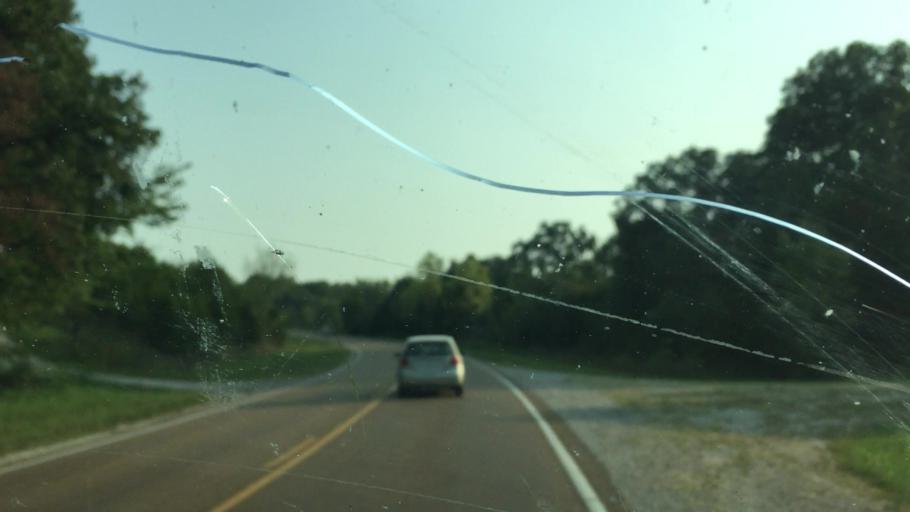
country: US
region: Missouri
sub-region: Pulaski County
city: Richland
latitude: 37.8177
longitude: -92.4068
